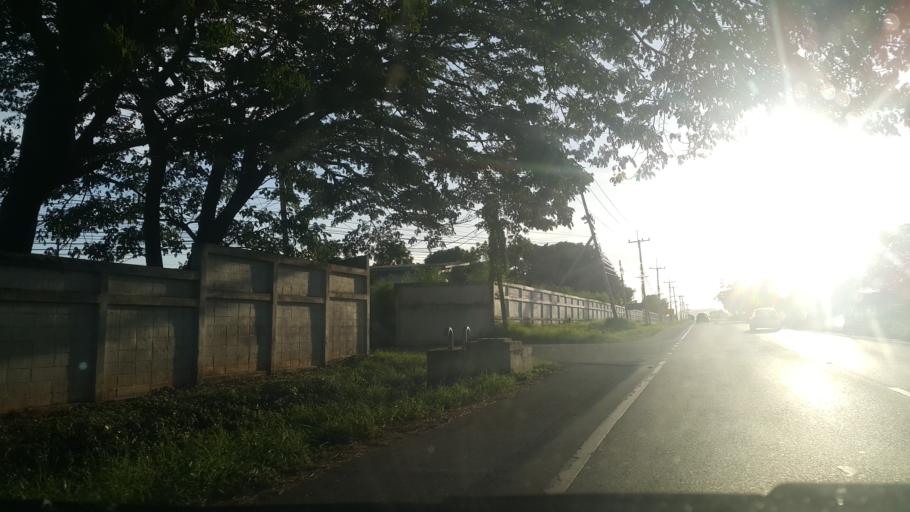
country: TH
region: Chon Buri
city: Sattahip
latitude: 12.6657
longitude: 100.9255
